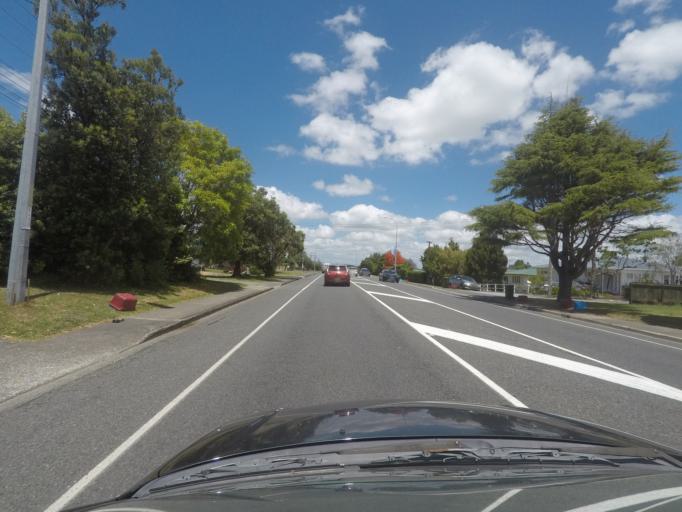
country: NZ
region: Northland
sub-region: Whangarei
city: Whangarei
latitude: -35.7481
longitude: 174.3674
